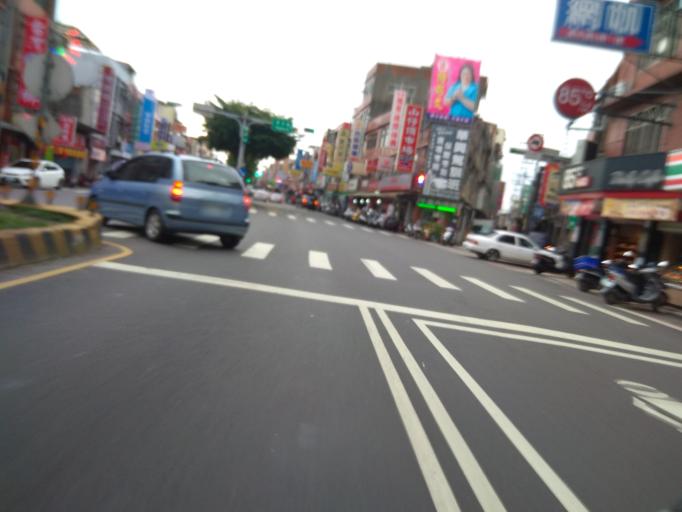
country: TW
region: Taiwan
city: Daxi
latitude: 24.8993
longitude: 121.2108
